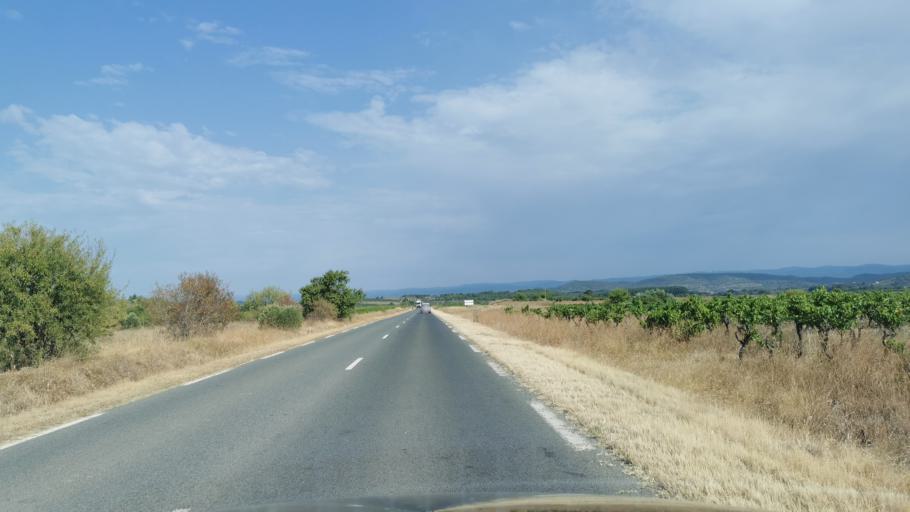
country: FR
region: Languedoc-Roussillon
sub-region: Departement de l'Aude
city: Ginestas
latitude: 43.2788
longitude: 2.8817
